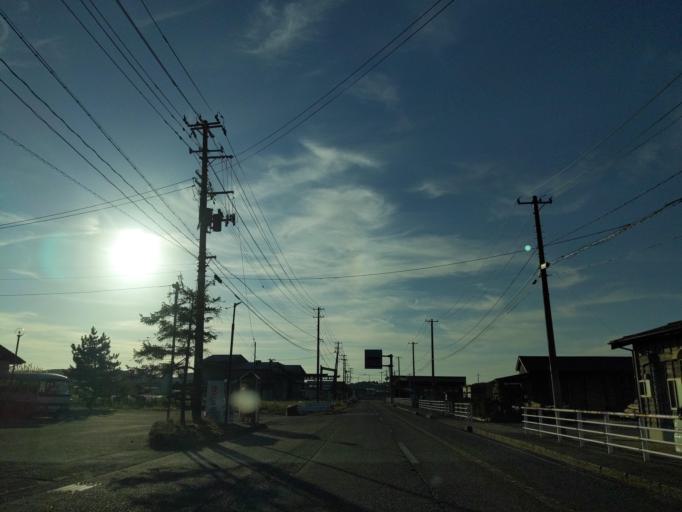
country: JP
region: Niigata
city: Yoshida-kasugacho
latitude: 37.5807
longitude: 138.7817
